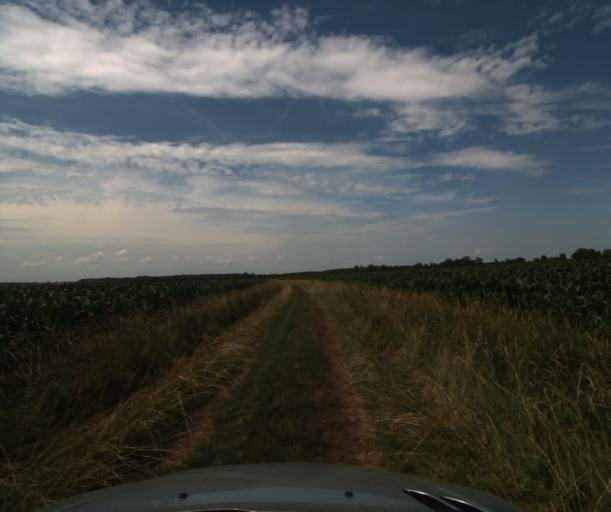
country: FR
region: Midi-Pyrenees
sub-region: Departement de la Haute-Garonne
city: Labastidette
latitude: 43.4787
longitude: 1.2229
